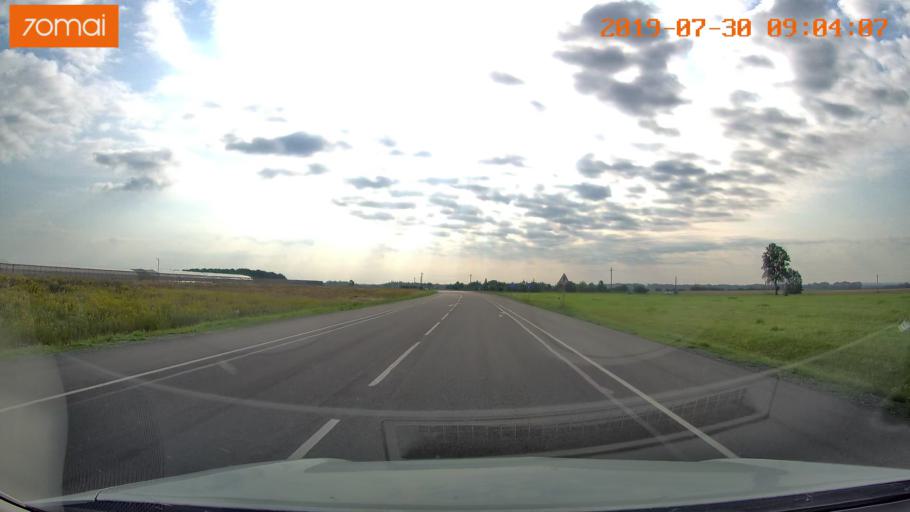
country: RU
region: Kaliningrad
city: Gusev
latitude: 54.6051
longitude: 22.2716
